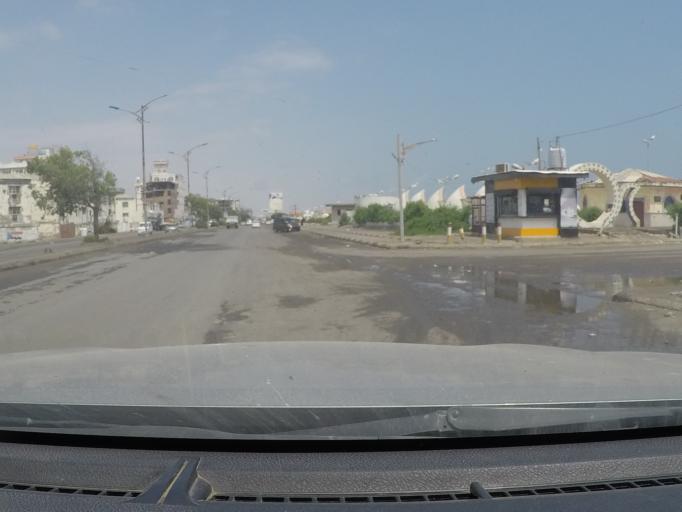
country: YE
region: Aden
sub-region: Khur Maksar
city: Khawr Maksar
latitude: 12.8141
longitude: 45.0422
